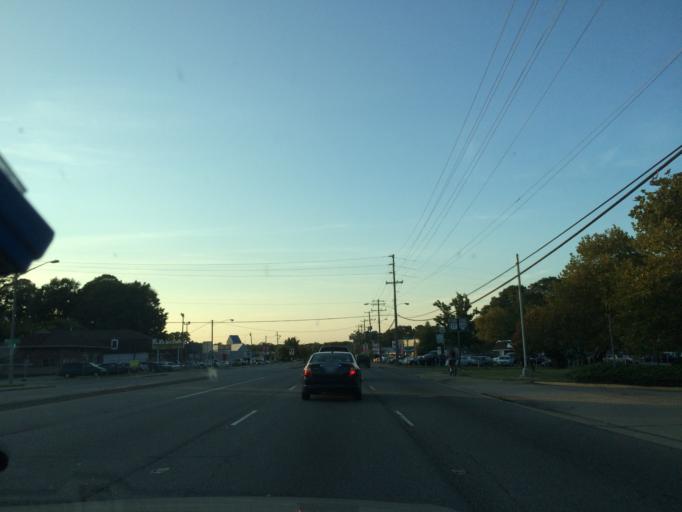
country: US
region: Virginia
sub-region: City of Newport News
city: Newport News
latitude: 37.0376
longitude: -76.4558
